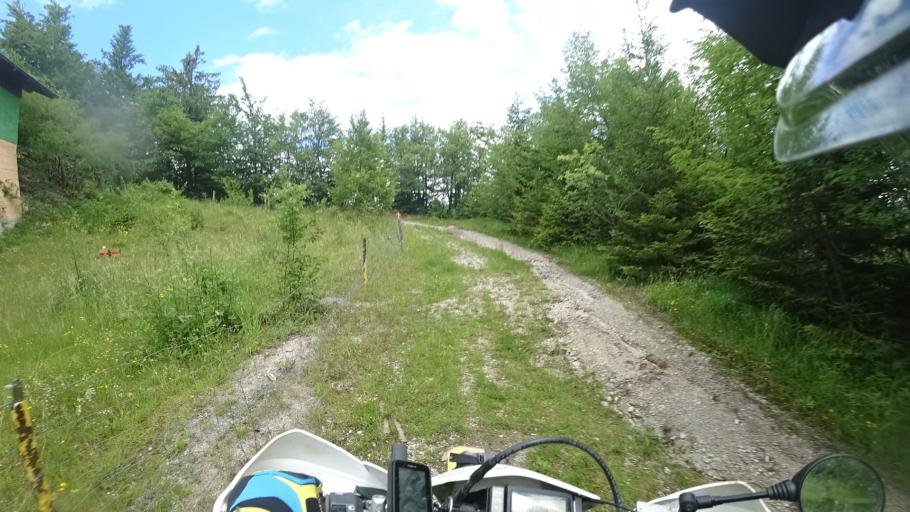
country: SI
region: Osilnica
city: Osilnica
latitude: 45.5949
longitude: 14.6294
